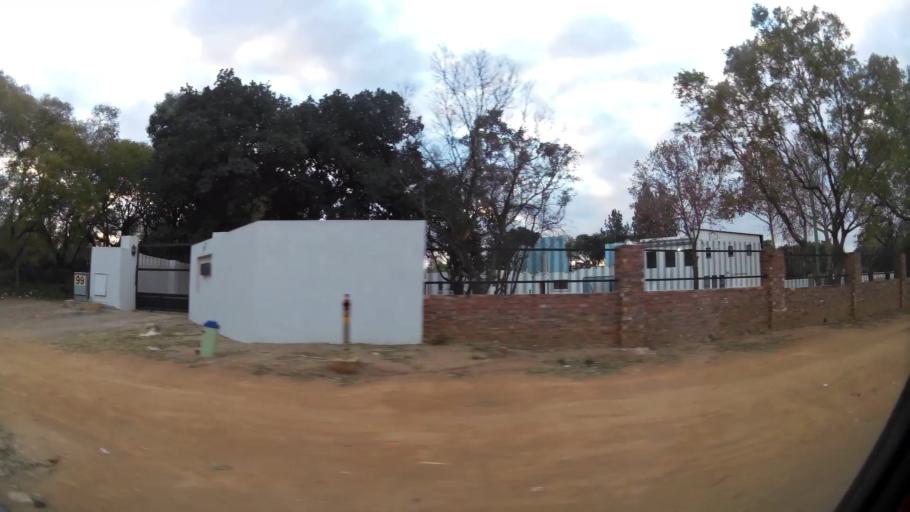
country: ZA
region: Gauteng
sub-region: City of Johannesburg Metropolitan Municipality
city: Midrand
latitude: -25.9857
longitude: 28.1575
